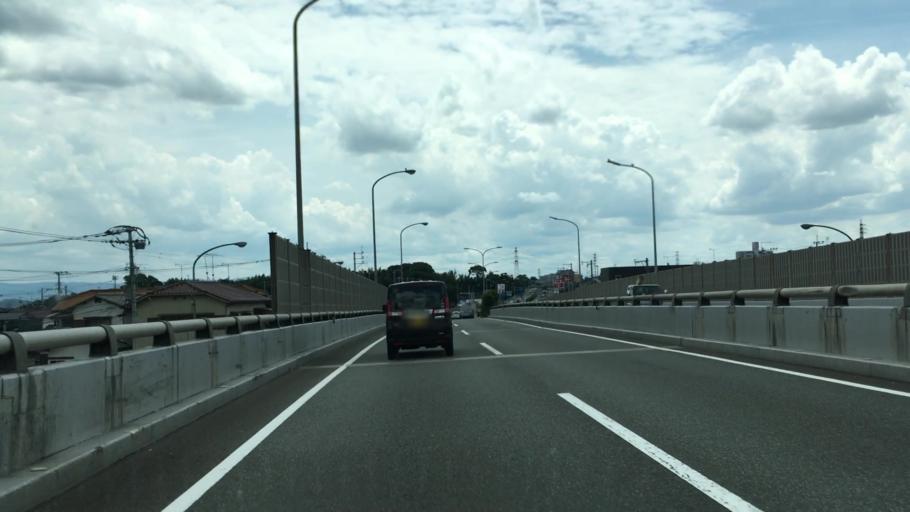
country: JP
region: Fukuoka
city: Chikushino-shi
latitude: 33.4828
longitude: 130.5382
